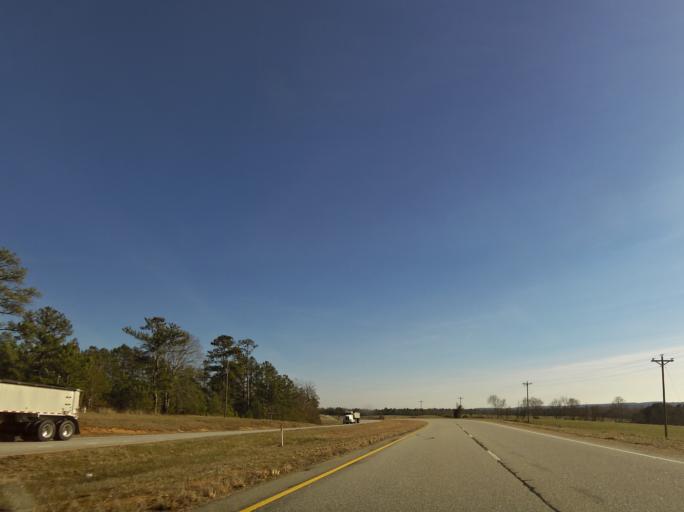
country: US
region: Georgia
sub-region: Upson County
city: Thomaston
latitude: 32.7525
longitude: -84.2427
